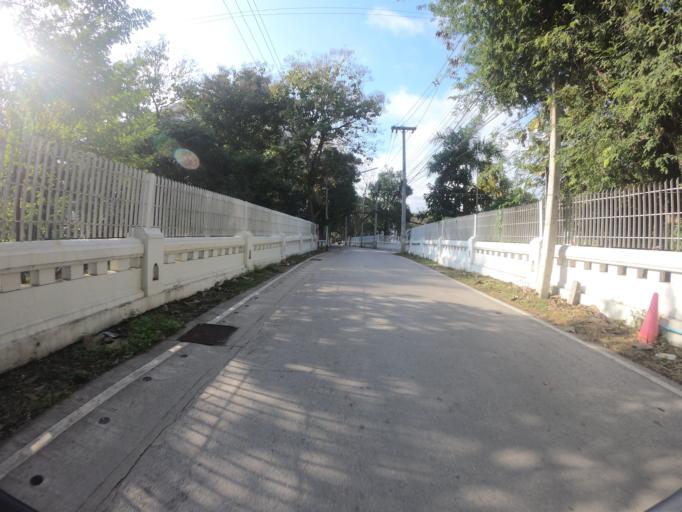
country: TH
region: Chiang Mai
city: Chiang Mai
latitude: 18.8115
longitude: 98.9548
